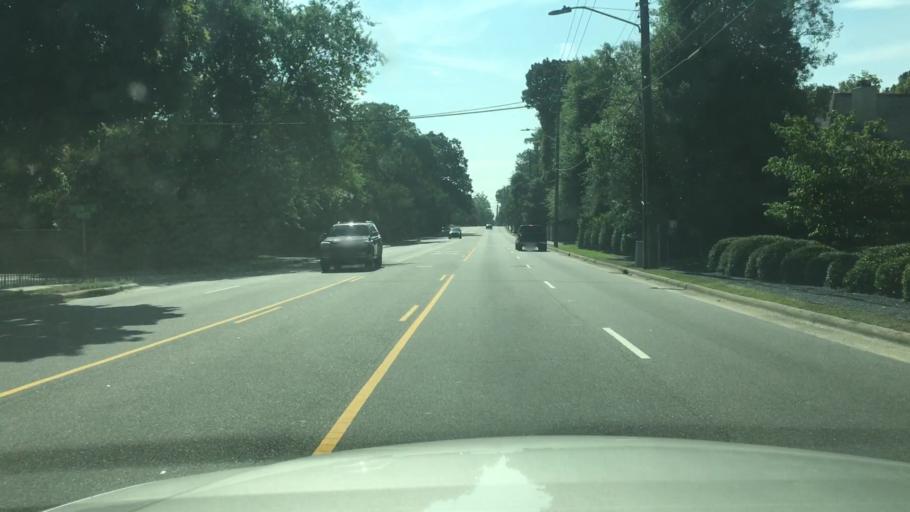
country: US
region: North Carolina
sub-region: Cumberland County
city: Fayetteville
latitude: 35.0591
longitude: -78.9085
